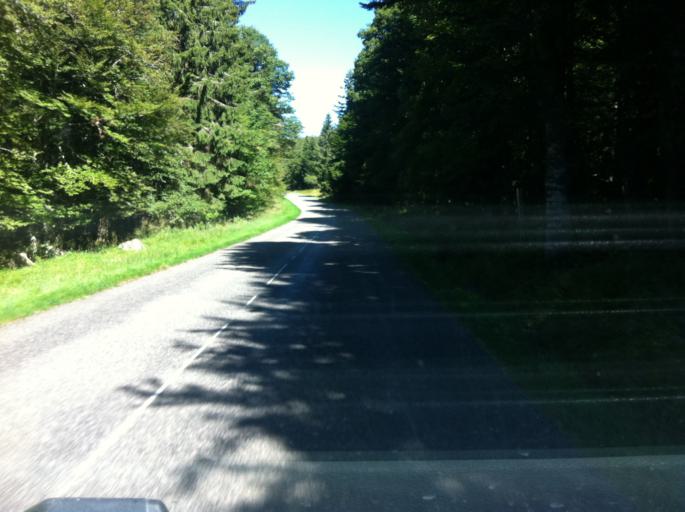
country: FR
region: Alsace
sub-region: Departement du Haut-Rhin
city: Soultzeren
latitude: 48.1262
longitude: 7.0732
